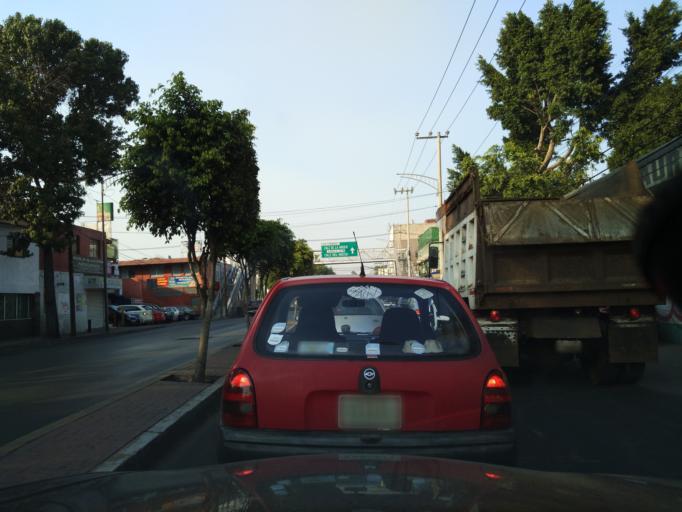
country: MX
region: Mexico City
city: Xochimilco
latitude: 19.2942
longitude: -99.1146
